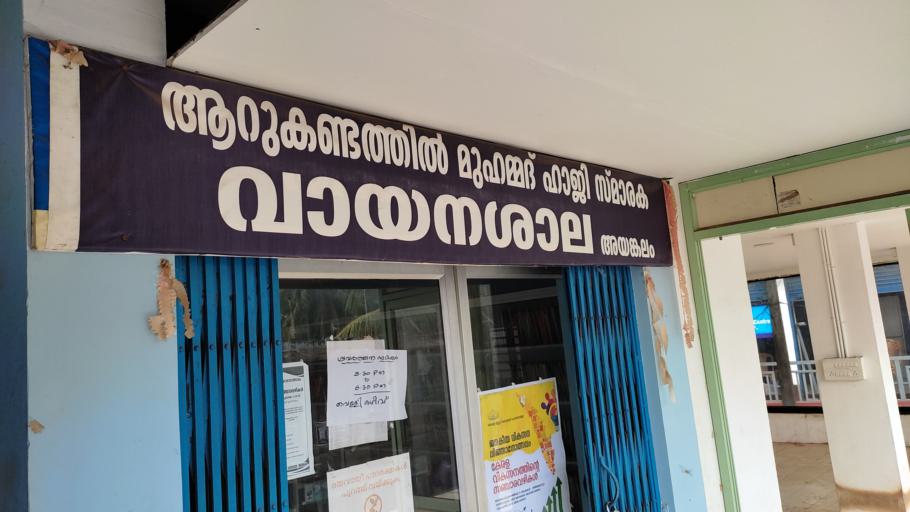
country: IN
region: Kerala
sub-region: Malappuram
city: Ponnani
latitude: 10.8412
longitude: 75.9948
